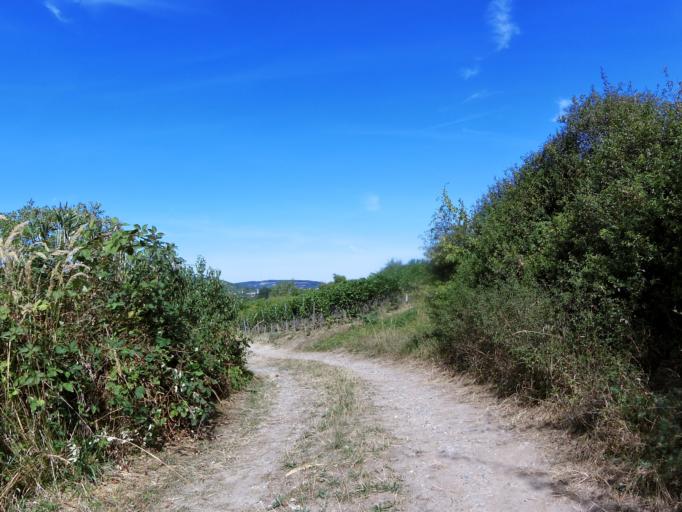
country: DE
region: Bavaria
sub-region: Regierungsbezirk Unterfranken
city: Randersacker
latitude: 49.7445
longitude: 9.9947
